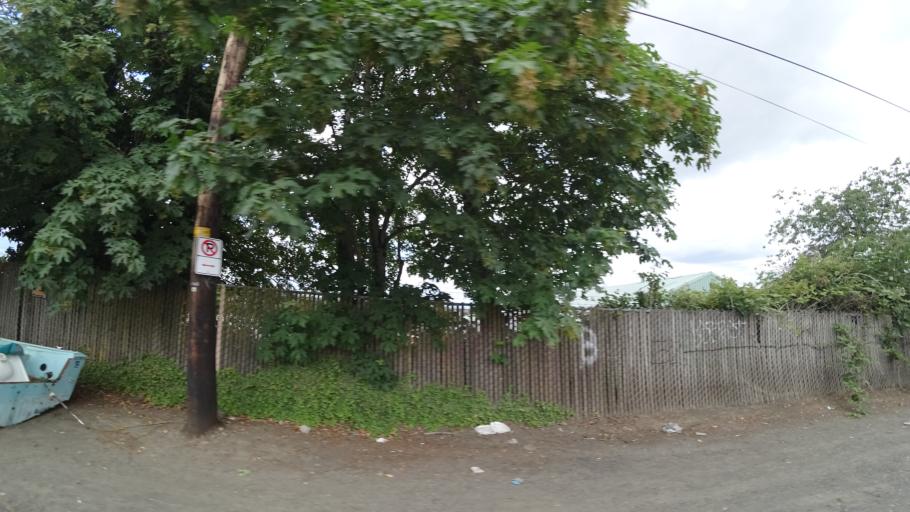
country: US
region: Oregon
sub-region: Multnomah County
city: Lents
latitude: 45.5654
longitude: -122.5918
